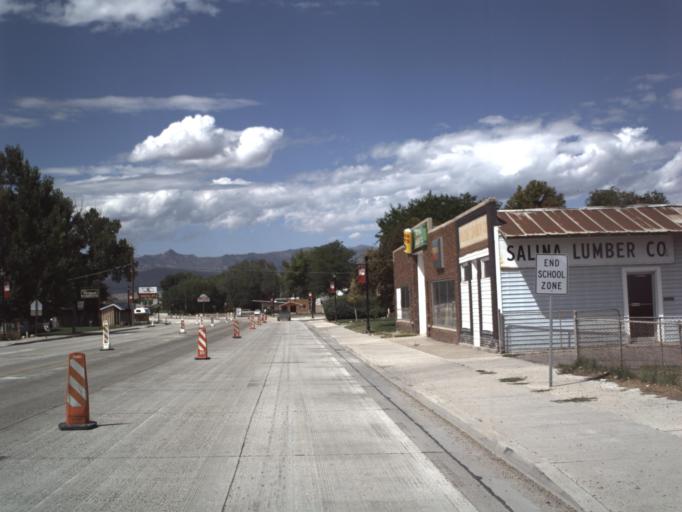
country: US
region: Utah
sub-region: Sevier County
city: Salina
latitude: 38.9576
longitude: -111.8609
